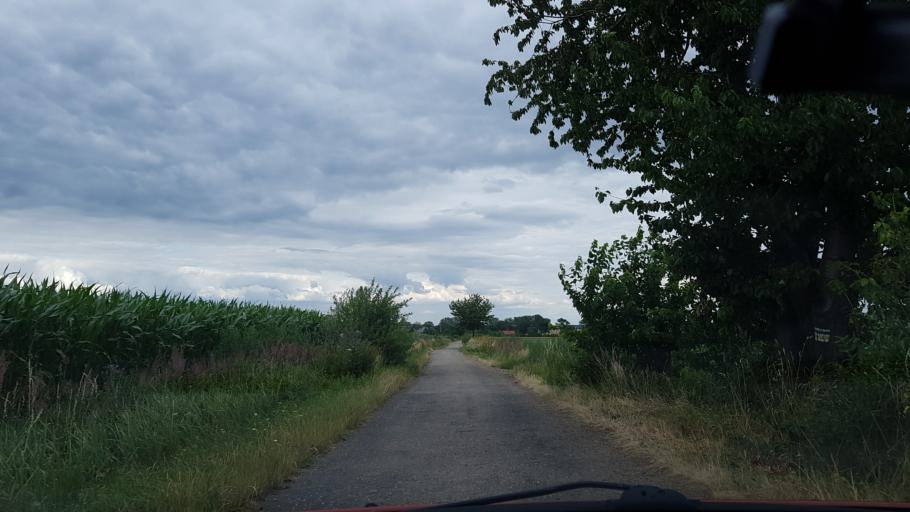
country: PL
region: Lower Silesian Voivodeship
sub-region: Powiat zabkowicki
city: Zabkowice Slaskie
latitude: 50.5711
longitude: 16.7777
